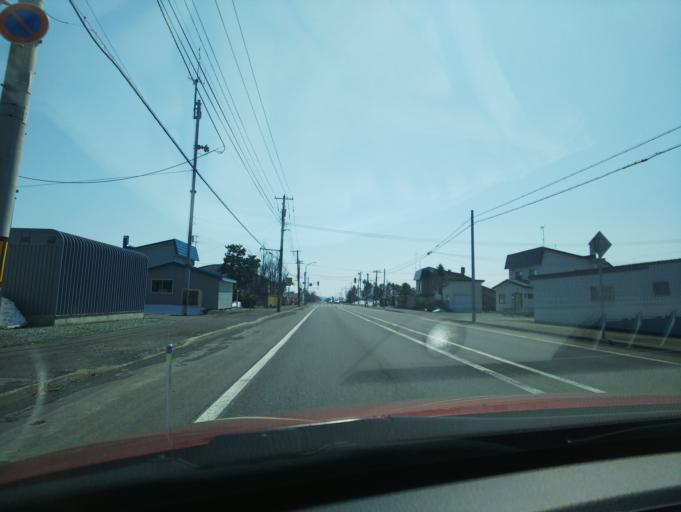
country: JP
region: Hokkaido
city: Nayoro
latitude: 44.2369
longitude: 142.3948
